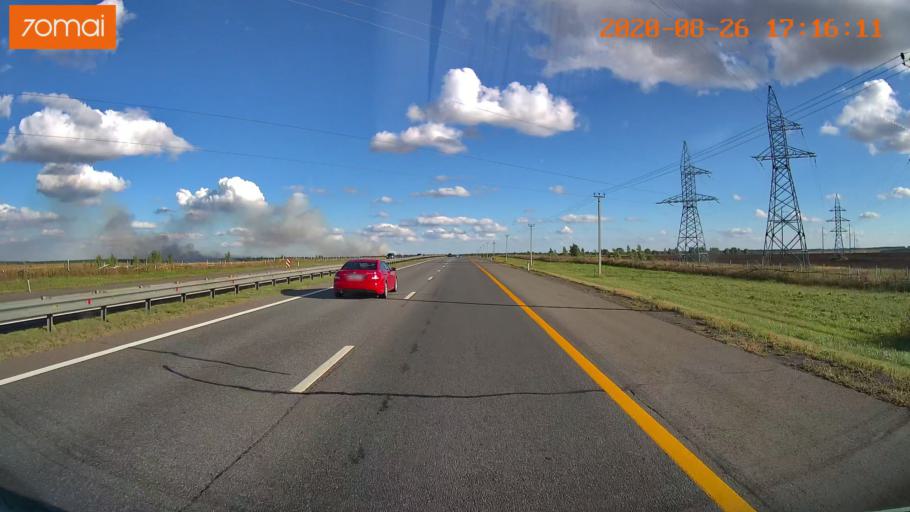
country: RU
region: Tula
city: Volovo
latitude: 53.6397
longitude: 38.0679
